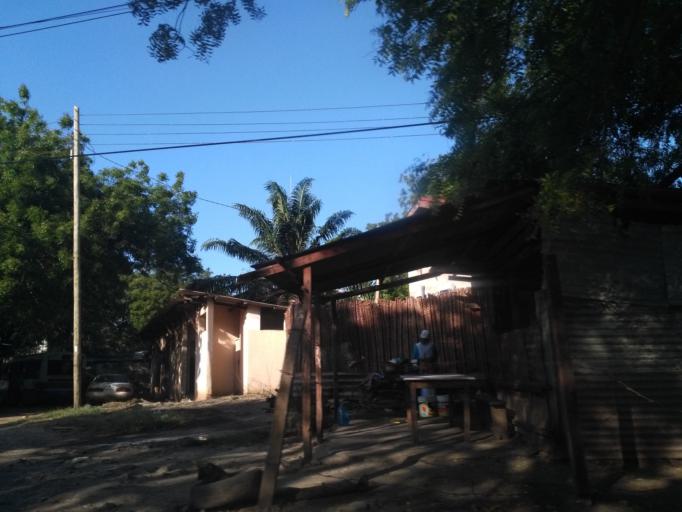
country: TZ
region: Dar es Salaam
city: Magomeni
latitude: -6.7857
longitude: 39.2763
